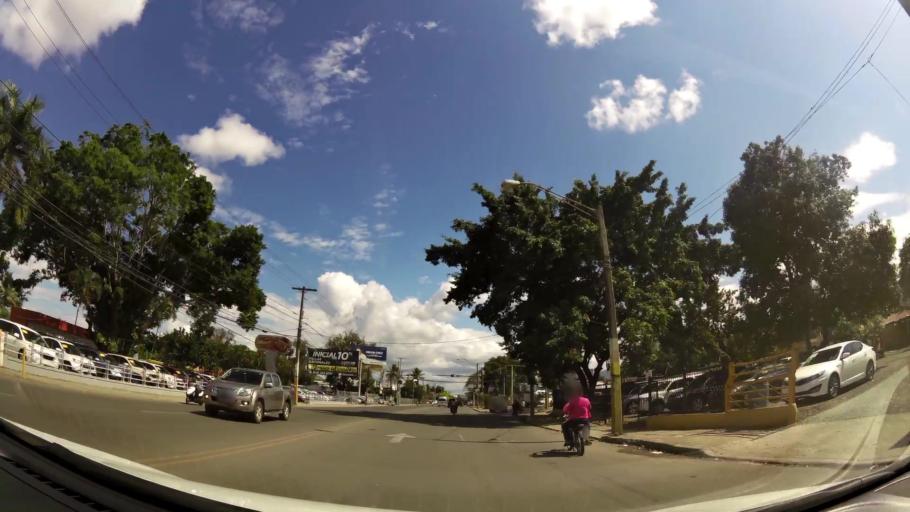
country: DO
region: La Vega
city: Concepcion de La Vega
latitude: 19.2337
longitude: -70.5306
